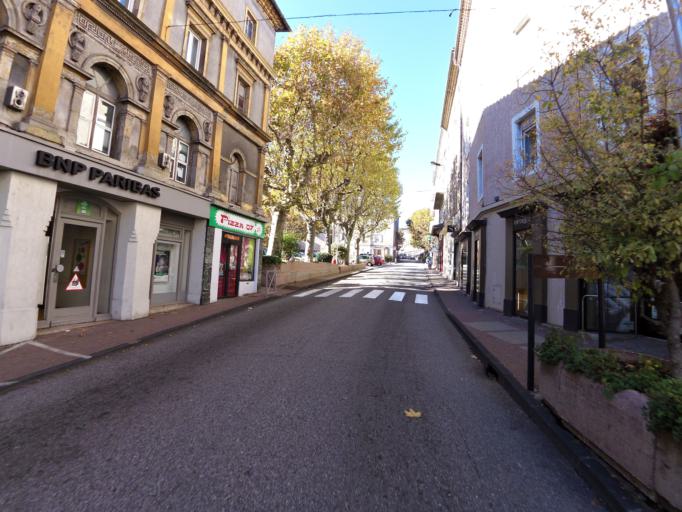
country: FR
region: Rhone-Alpes
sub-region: Departement de l'Ardeche
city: Privas
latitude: 44.7347
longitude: 4.5978
